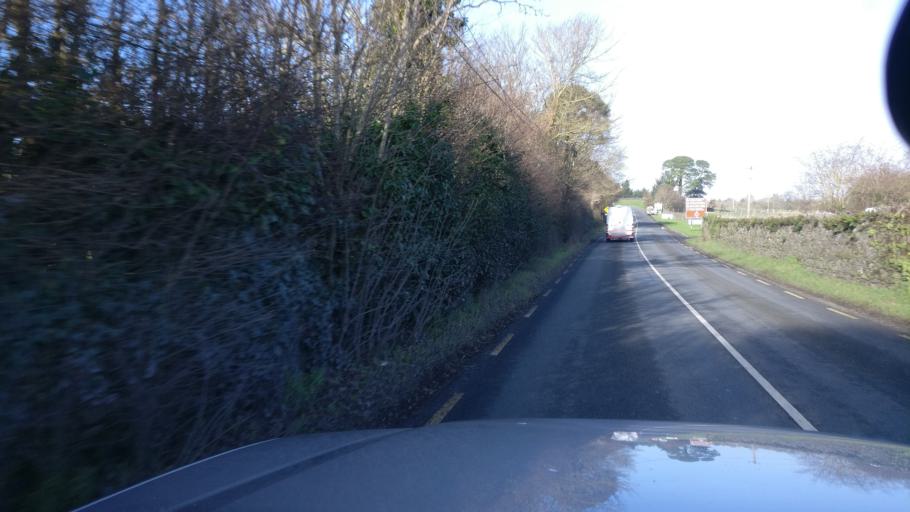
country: IE
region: Leinster
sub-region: Kilkenny
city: Kilkenny
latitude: 52.6376
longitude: -7.2274
